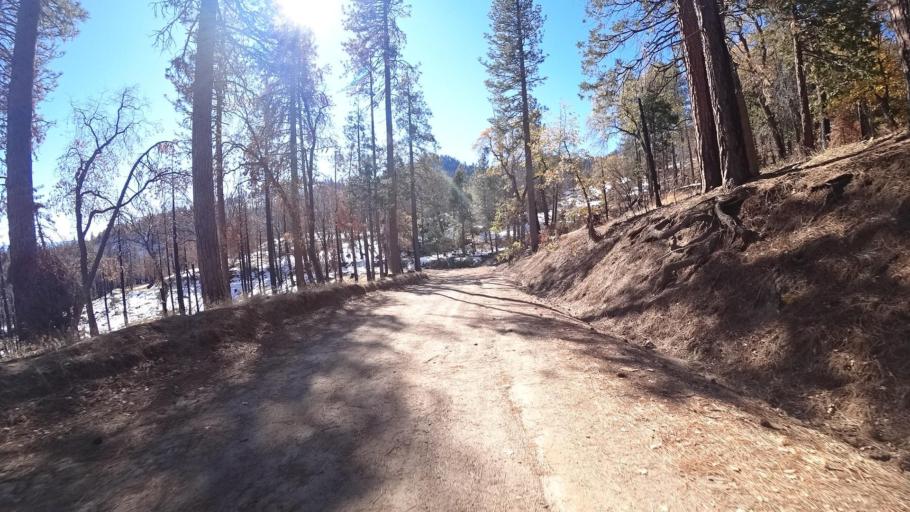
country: US
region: California
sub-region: Kern County
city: Alta Sierra
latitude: 35.7212
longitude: -118.5442
